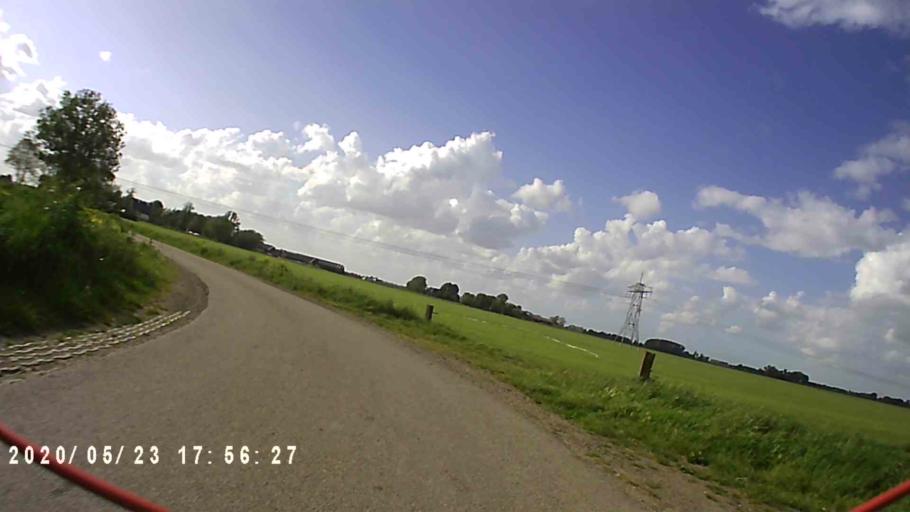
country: NL
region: Groningen
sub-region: Gemeente Slochteren
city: Slochteren
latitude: 53.2505
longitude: 6.7452
